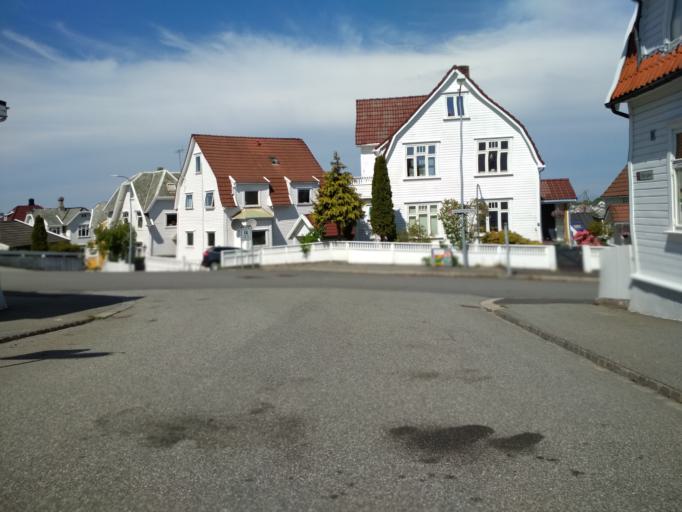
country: NO
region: Rogaland
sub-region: Stavanger
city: Stavanger
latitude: 58.9588
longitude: 5.7338
